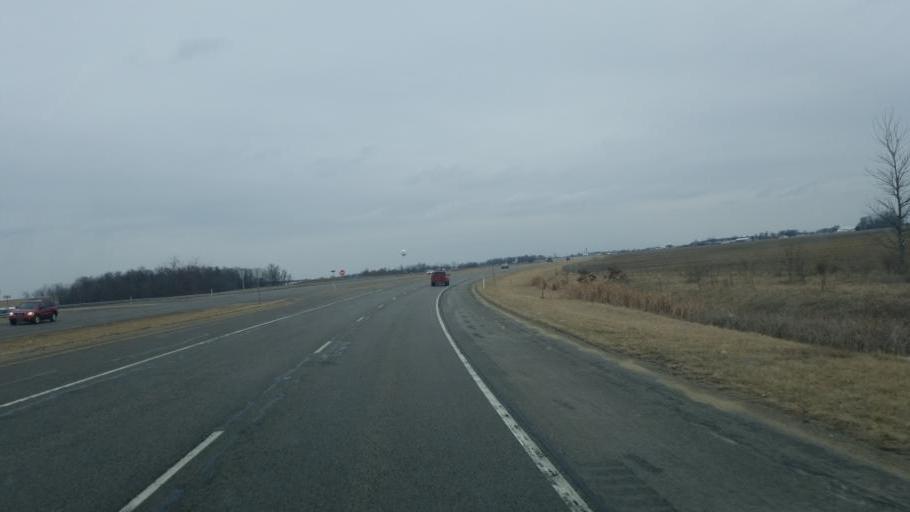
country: US
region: Indiana
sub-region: Adams County
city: Decatur
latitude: 40.7575
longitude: -84.9391
